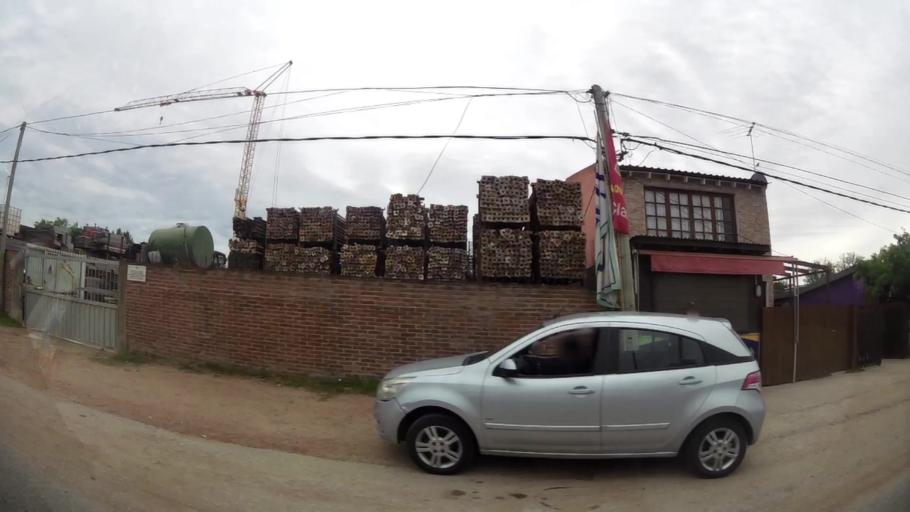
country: UY
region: Maldonado
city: Maldonado
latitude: -34.9096
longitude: -54.9432
